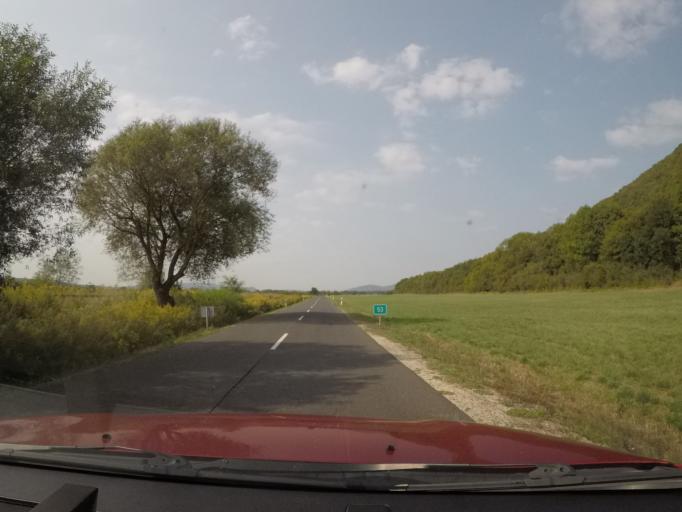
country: SK
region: Kosicky
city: Medzev
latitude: 48.5721
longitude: 20.8330
